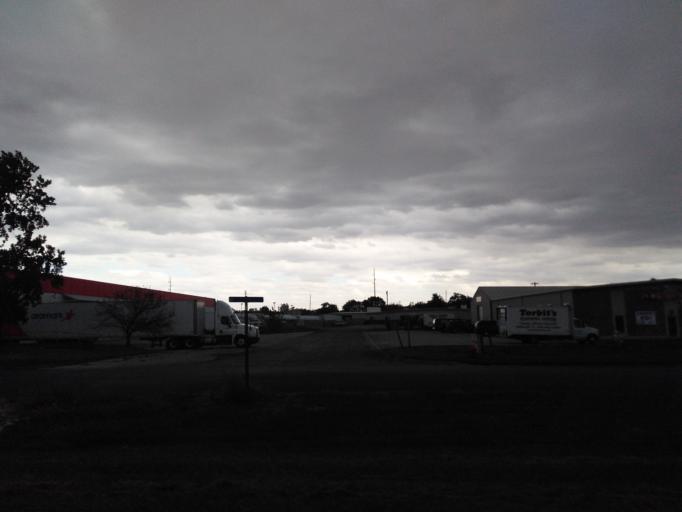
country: US
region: Illinois
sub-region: Madison County
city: Highland
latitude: 38.7432
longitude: -89.6916
